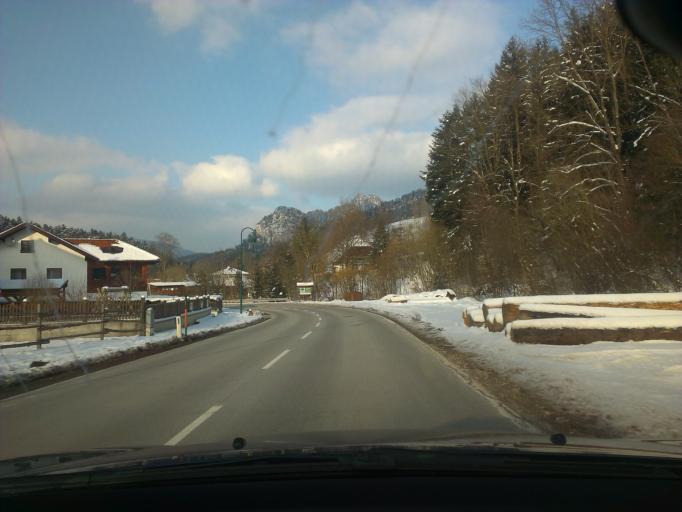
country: AT
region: Lower Austria
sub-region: Politischer Bezirk Wiener Neustadt
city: Miesenbach
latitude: 47.8452
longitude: 15.9834
